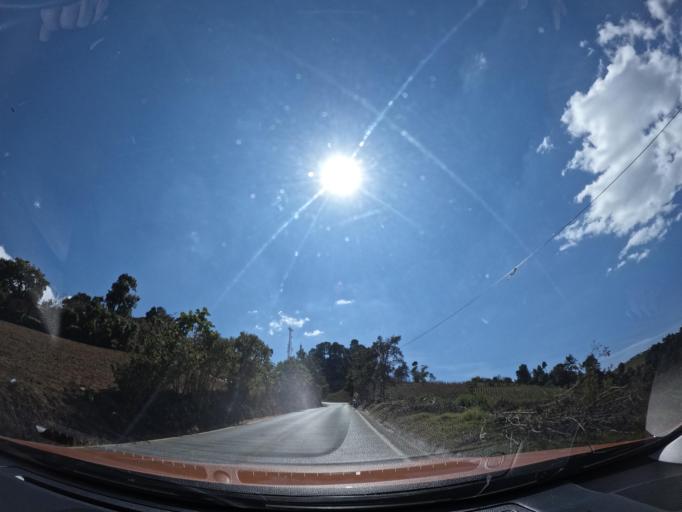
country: GT
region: Chimaltenango
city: Patzun
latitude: 14.6725
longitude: -91.0573
